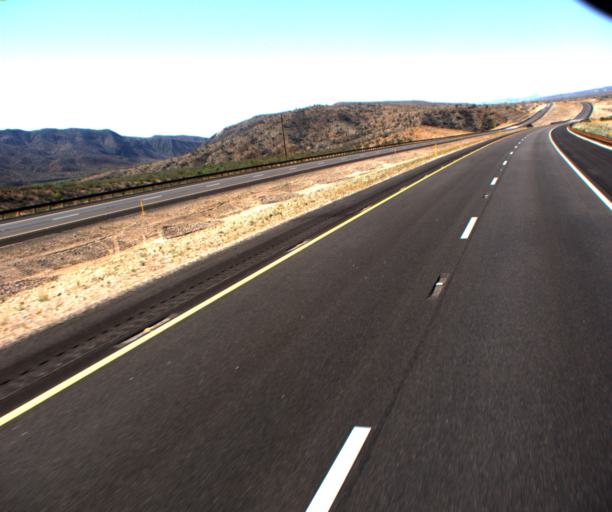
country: US
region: Arizona
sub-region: Mohave County
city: Kingman
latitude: 34.9965
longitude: -113.6646
